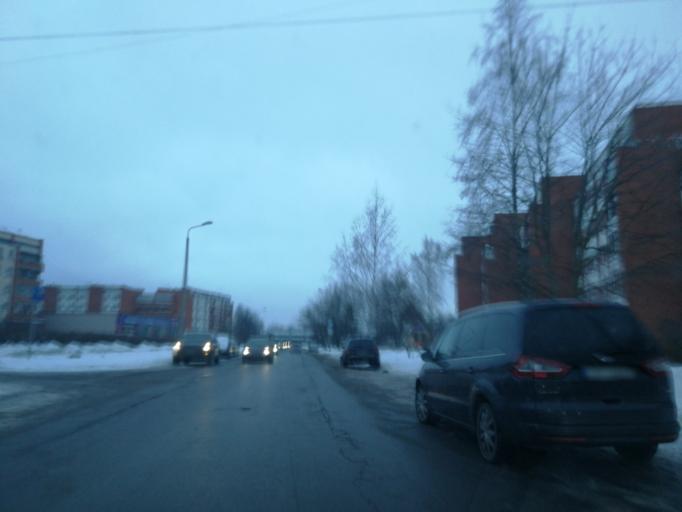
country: LV
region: Riga
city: Riga
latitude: 56.9441
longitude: 24.1732
